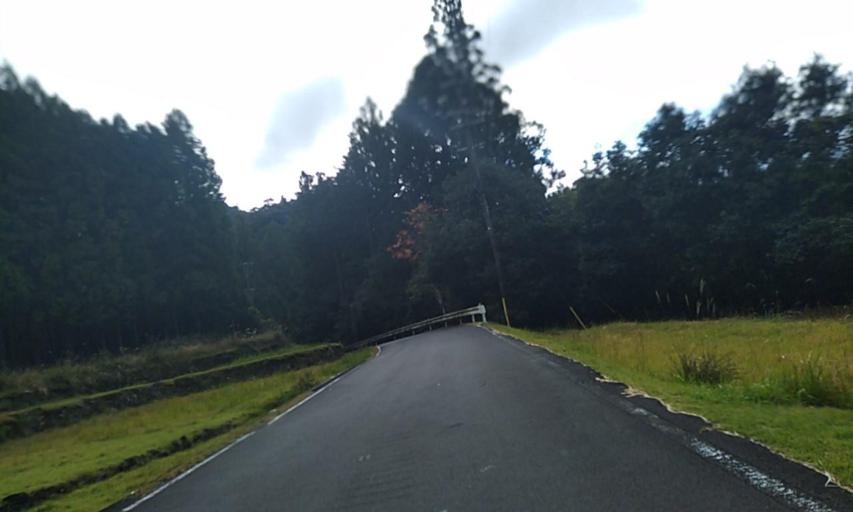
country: JP
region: Wakayama
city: Shingu
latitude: 33.9330
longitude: 135.9783
